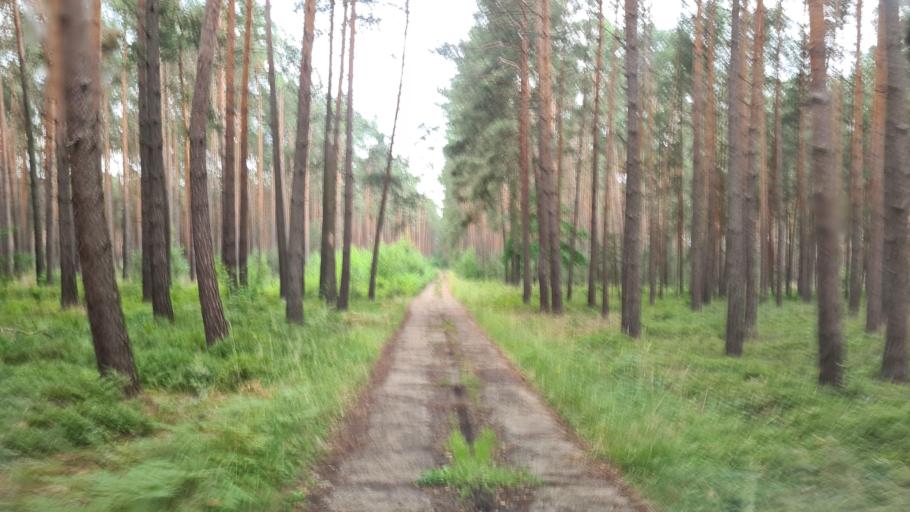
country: DE
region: Brandenburg
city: Crinitz
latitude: 51.7212
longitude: 13.7212
